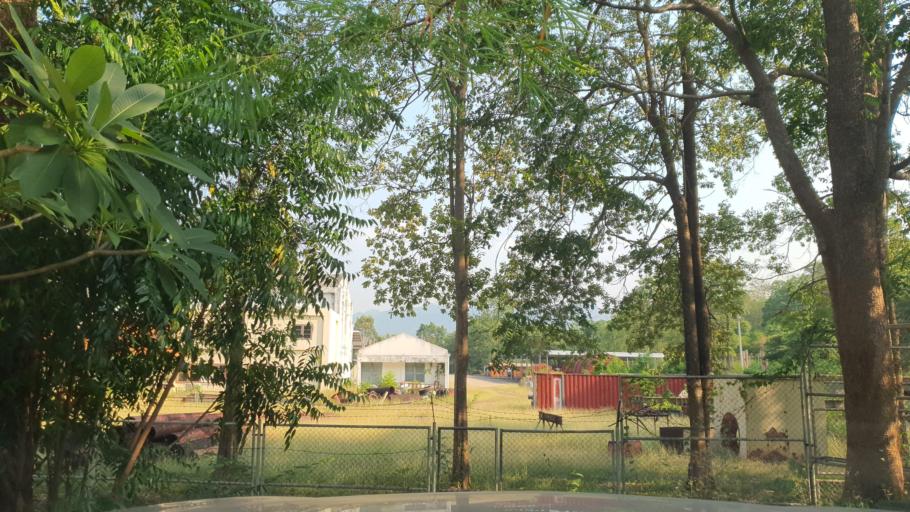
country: TH
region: Kanchanaburi
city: Sai Yok
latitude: 14.2253
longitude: 99.2240
